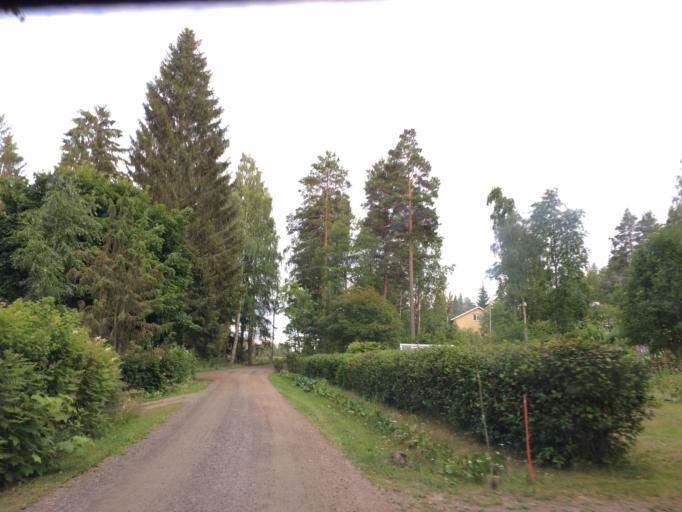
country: FI
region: Haeme
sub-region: Haemeenlinna
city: Tervakoski
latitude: 60.8553
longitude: 24.6233
